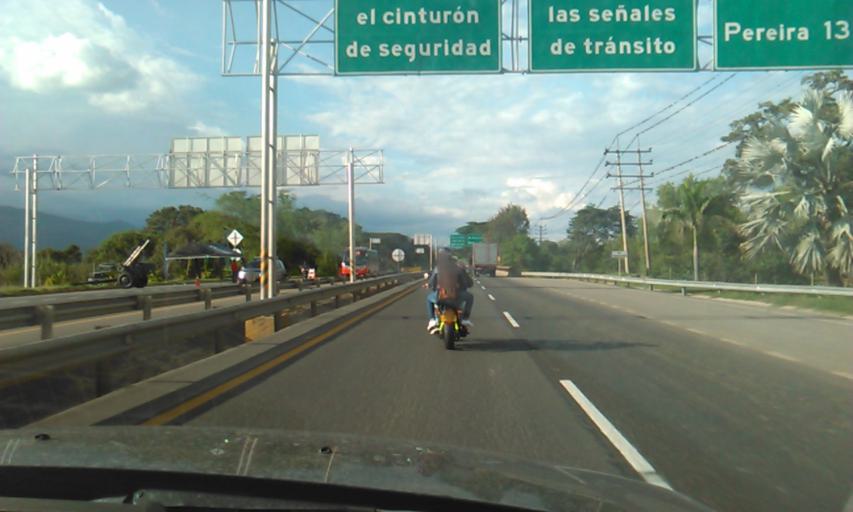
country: CO
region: Valle del Cauca
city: Buga
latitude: 3.8963
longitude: -76.3124
